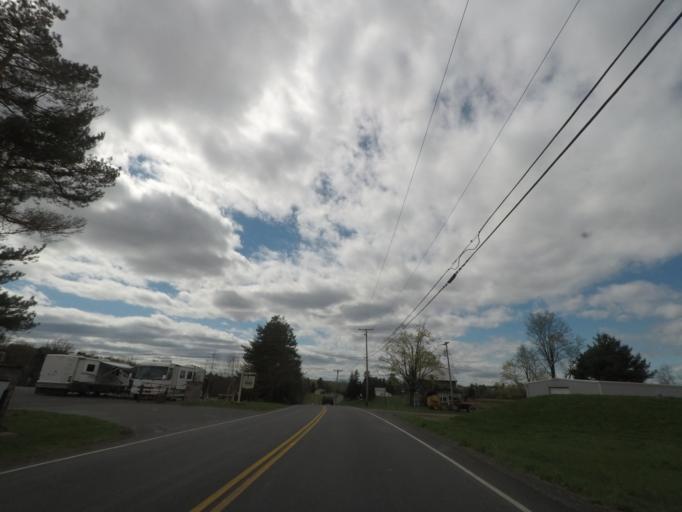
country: US
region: New York
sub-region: Columbia County
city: Valatie
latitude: 42.3997
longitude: -73.6625
